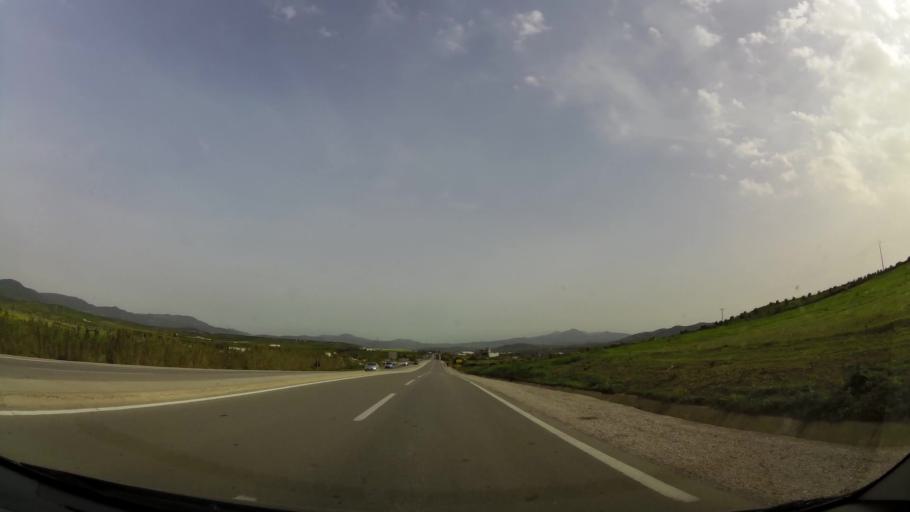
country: MA
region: Tanger-Tetouan
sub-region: Tanger-Assilah
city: Dar Chaoui
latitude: 35.6285
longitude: -5.6739
